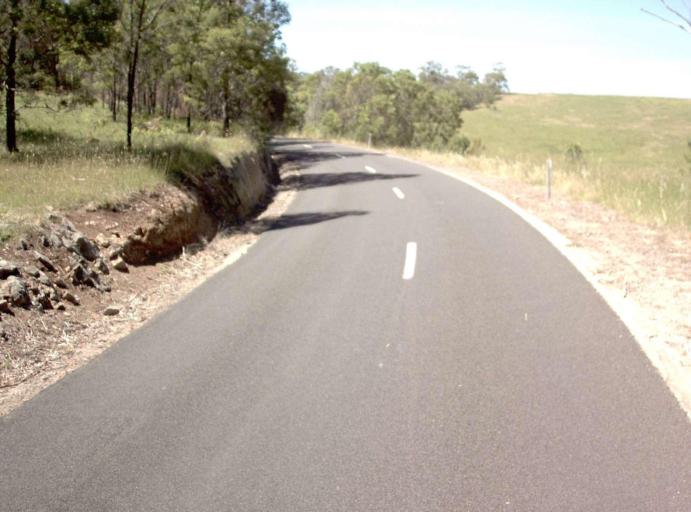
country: AU
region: Victoria
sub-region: East Gippsland
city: Lakes Entrance
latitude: -37.4448
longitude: 148.1908
